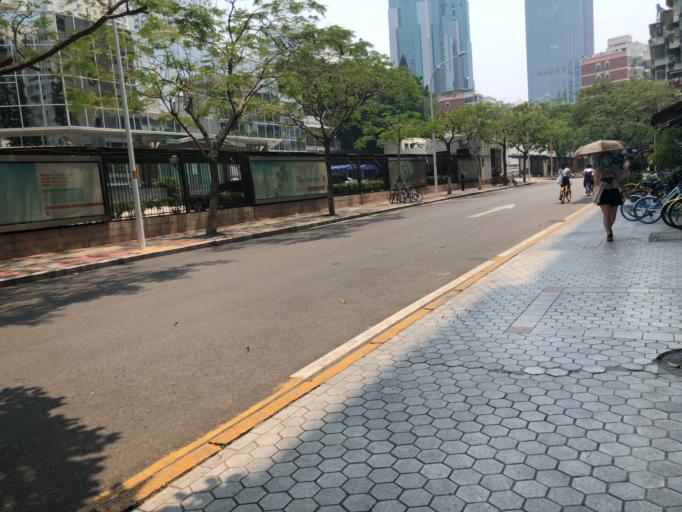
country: CN
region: Fujian
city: Xiamen
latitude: 24.4793
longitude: 118.0791
